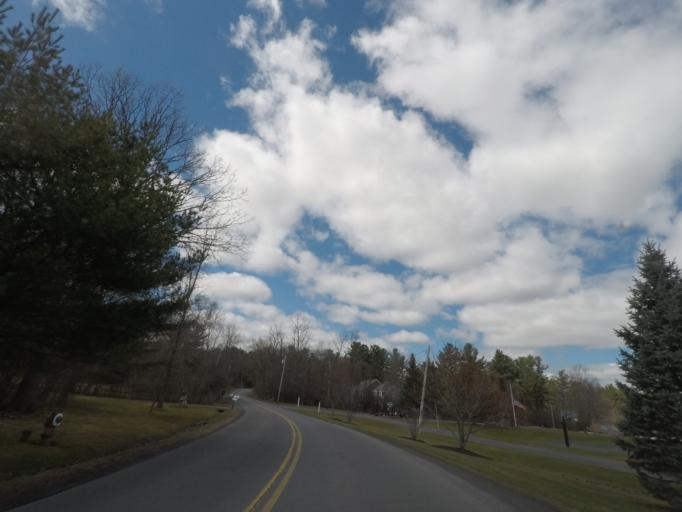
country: US
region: New York
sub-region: Albany County
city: Voorheesville
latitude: 42.6378
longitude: -73.9293
